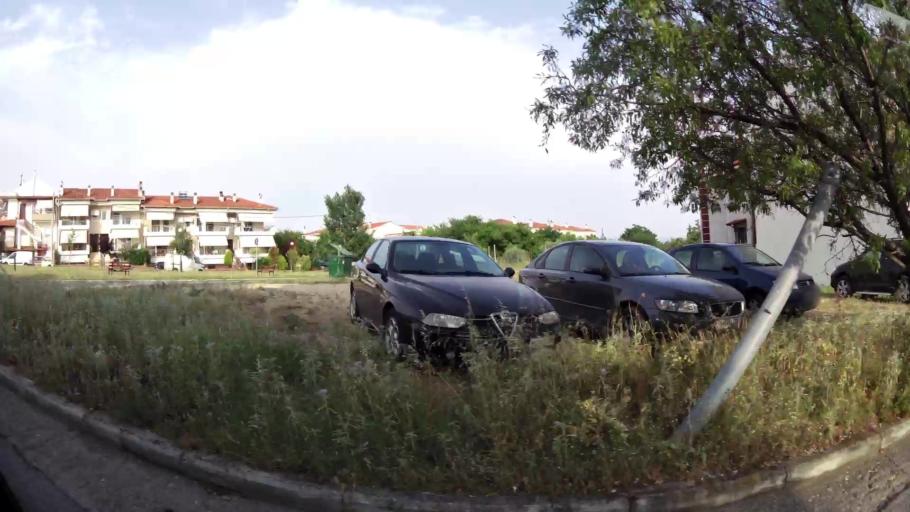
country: GR
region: Central Macedonia
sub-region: Nomos Thessalonikis
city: Oraiokastro
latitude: 40.7187
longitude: 22.9039
